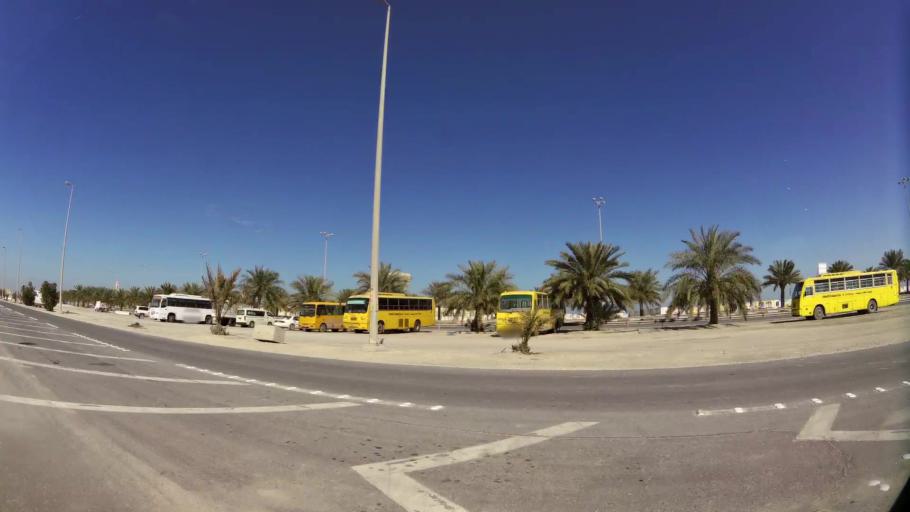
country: BH
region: Muharraq
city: Al Hadd
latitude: 26.2411
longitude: 50.6575
